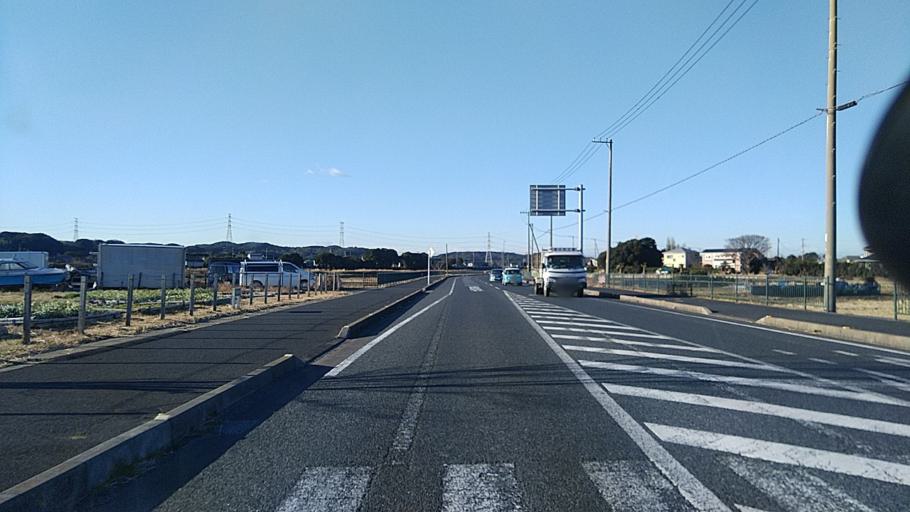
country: JP
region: Chiba
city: Kimitsu
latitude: 35.3241
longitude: 139.8889
